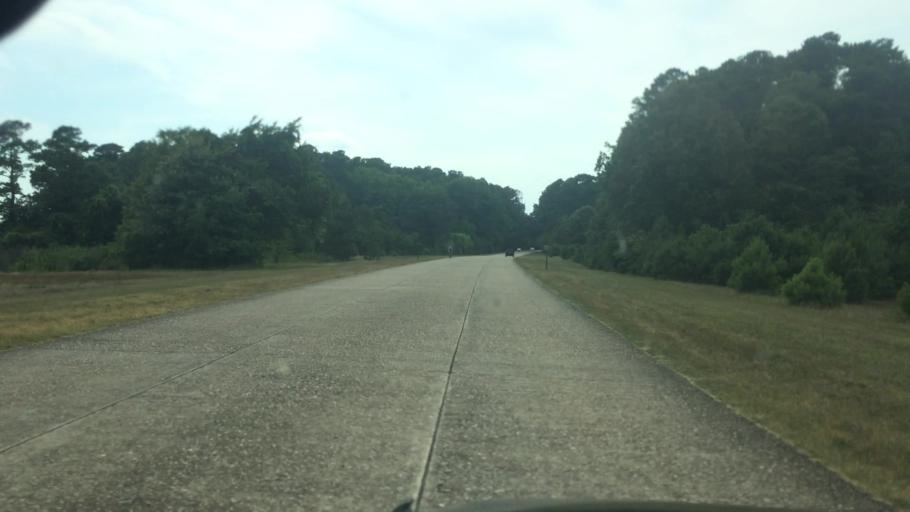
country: US
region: Virginia
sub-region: James City County
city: Williamsburg
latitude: 37.2136
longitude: -76.7371
